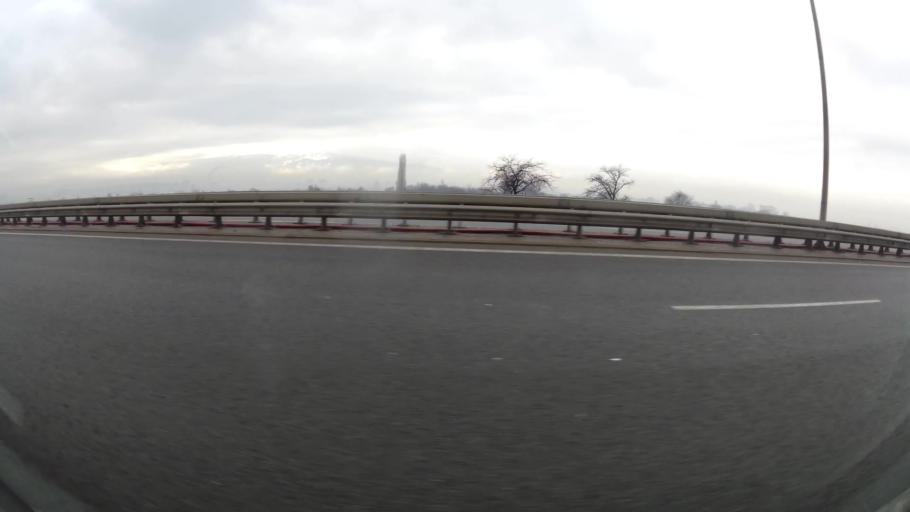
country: BG
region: Sofia-Capital
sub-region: Stolichna Obshtina
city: Sofia
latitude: 42.7285
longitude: 23.3799
